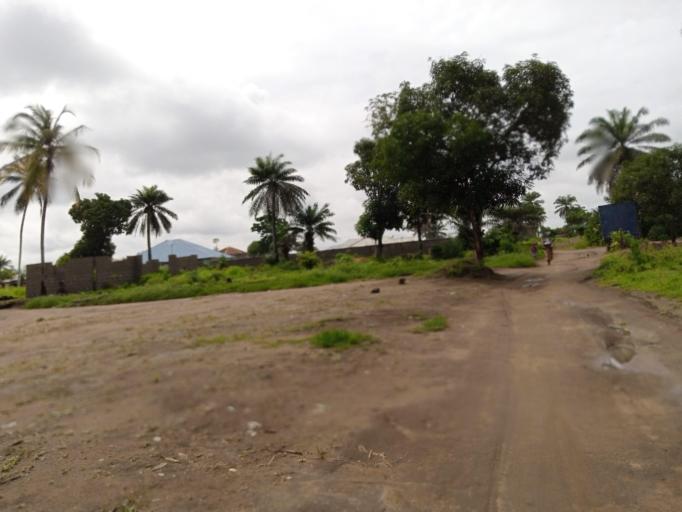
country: SL
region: Northern Province
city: Sawkta
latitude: 8.6269
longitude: -13.2000
